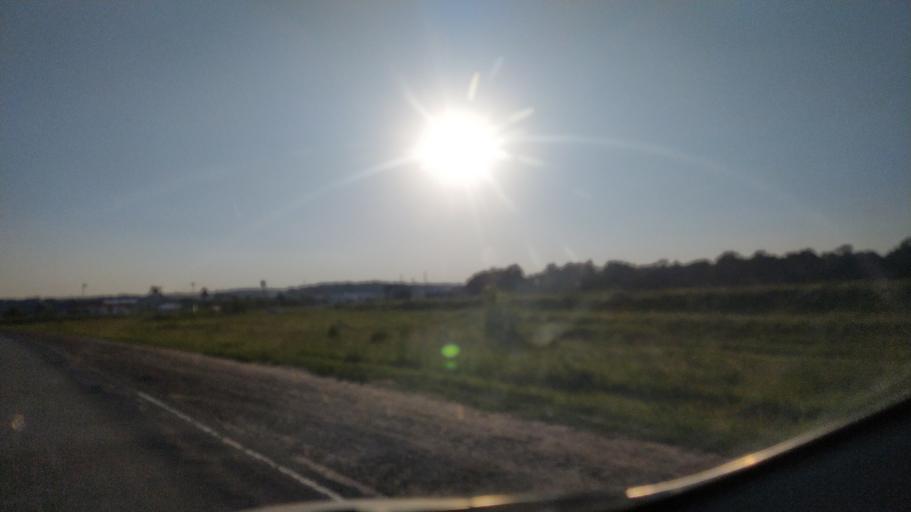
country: RU
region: Chuvashia
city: Kugesi
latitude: 56.0406
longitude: 47.3254
